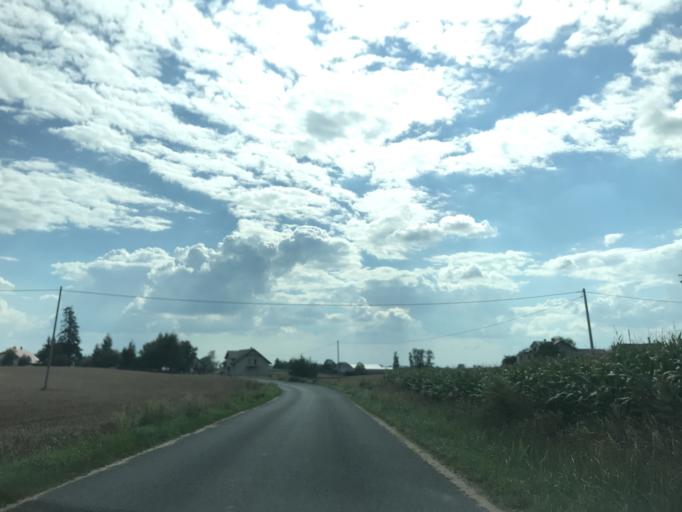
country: PL
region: Kujawsko-Pomorskie
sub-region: Powiat brodnicki
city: Brzozie
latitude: 53.3417
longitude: 19.6692
